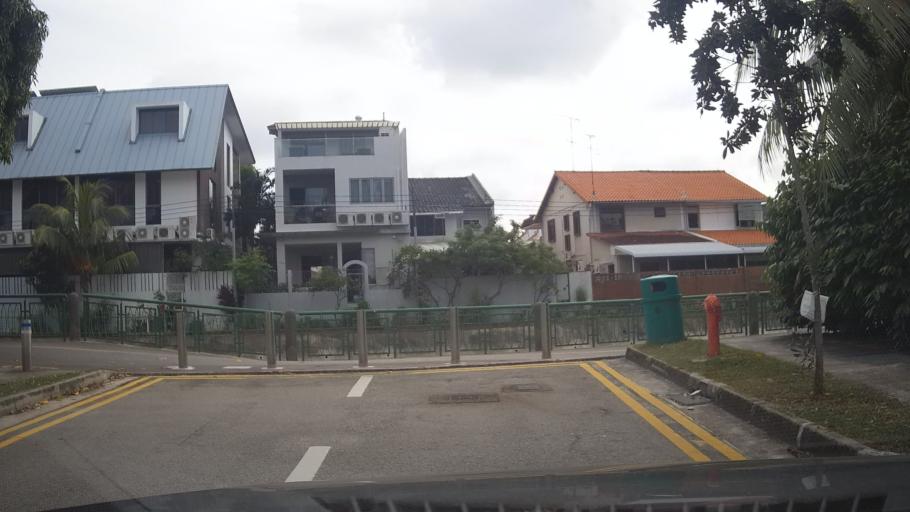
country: SG
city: Singapore
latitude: 1.3128
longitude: 103.9157
